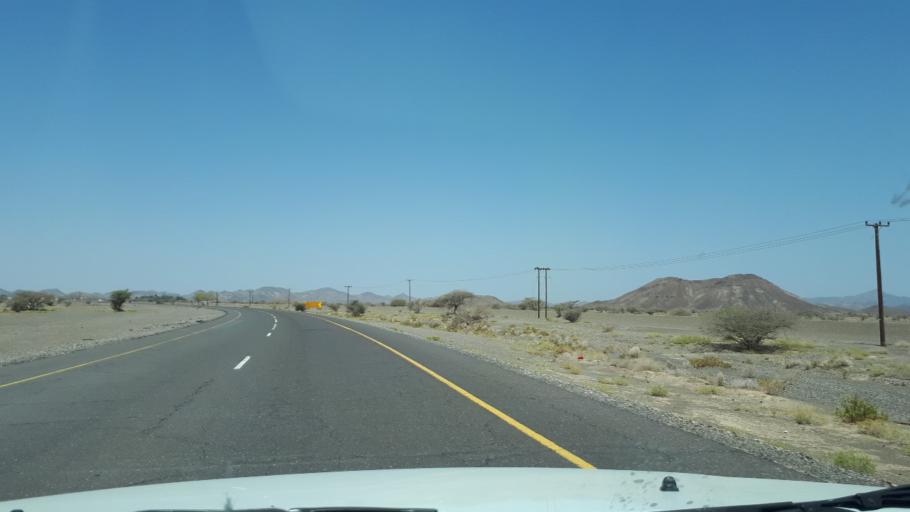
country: OM
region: Ash Sharqiyah
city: Ibra'
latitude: 22.6200
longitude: 58.4132
